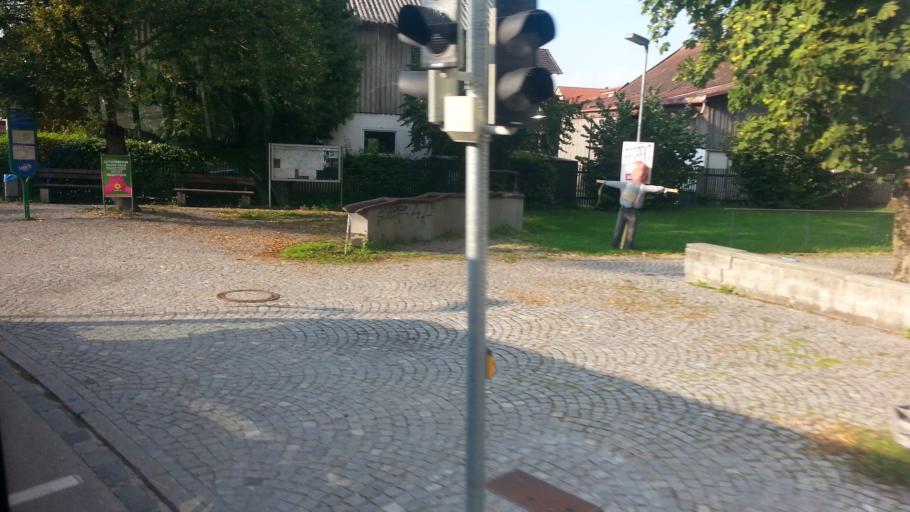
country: DE
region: Bavaria
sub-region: Upper Bavaria
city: Neufahrn bei Freising
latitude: 48.2809
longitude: 11.6739
